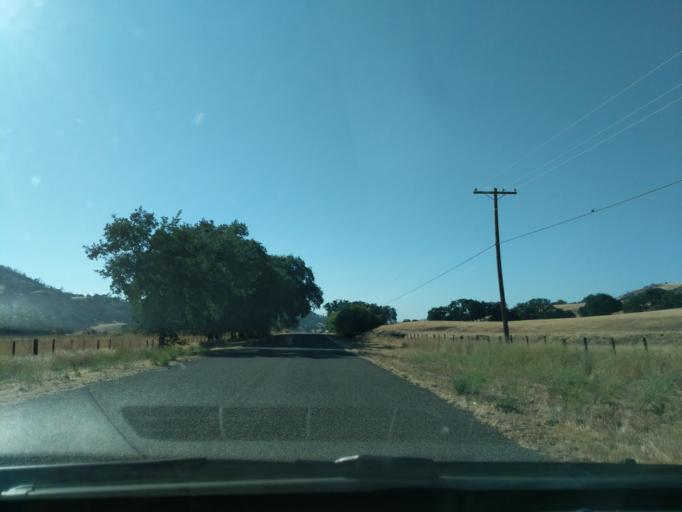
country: US
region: California
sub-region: San Luis Obispo County
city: San Miguel
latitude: 36.1162
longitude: -120.7273
